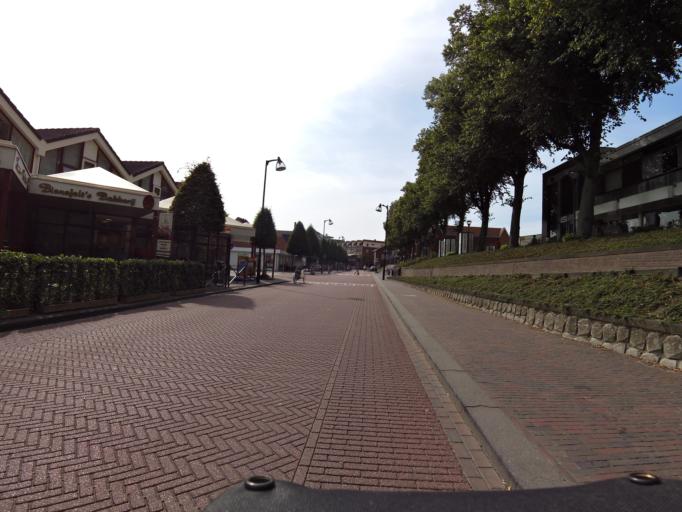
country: NL
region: South Holland
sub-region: Gemeente Goeree-Overflakkee
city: Middelharnis
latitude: 51.7606
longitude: 4.1580
